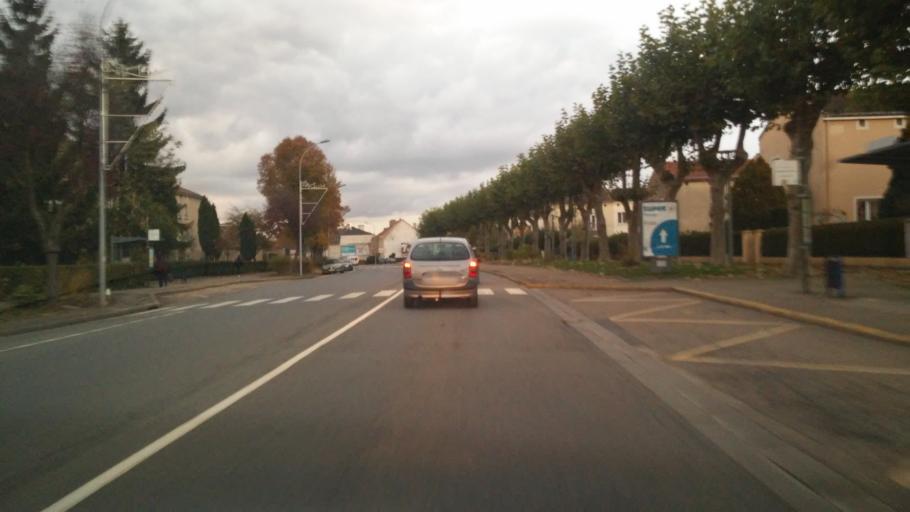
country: FR
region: Lorraine
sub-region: Departement de la Moselle
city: Maizieres-les-Metz
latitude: 49.2080
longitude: 6.1613
